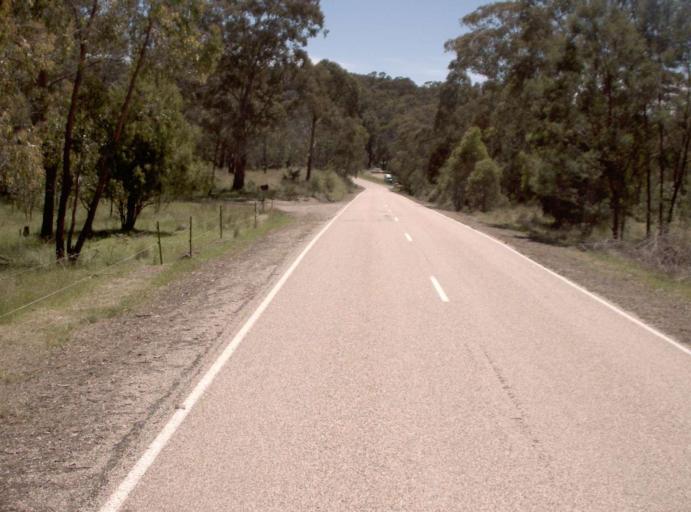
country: AU
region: Victoria
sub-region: East Gippsland
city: Lakes Entrance
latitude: -37.3239
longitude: 148.2422
